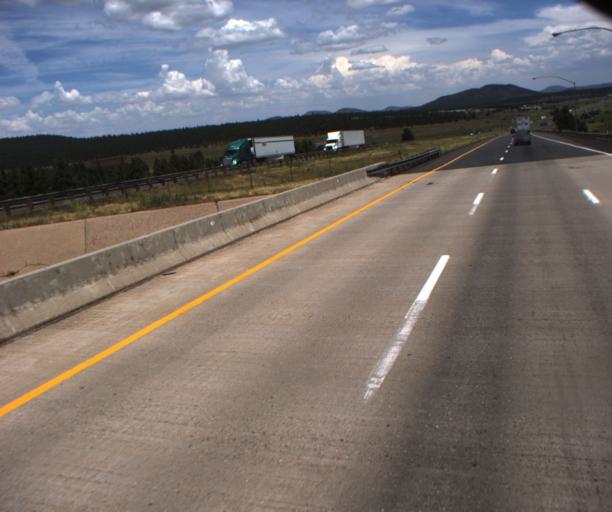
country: US
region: Arizona
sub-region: Coconino County
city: Williams
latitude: 35.2492
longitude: -112.2095
